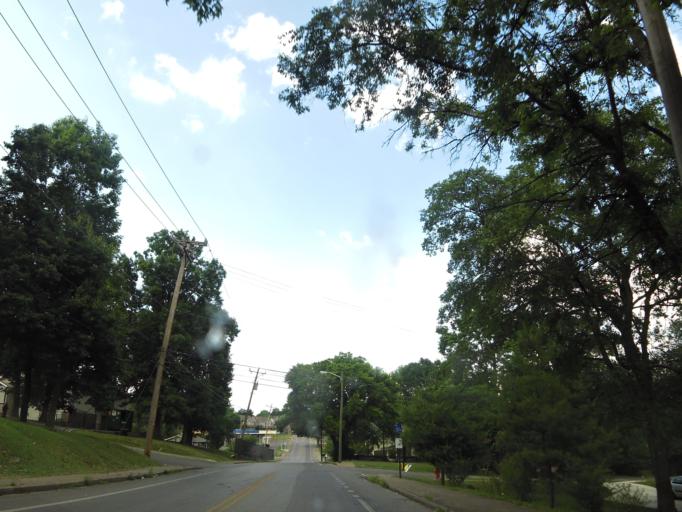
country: US
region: Tennessee
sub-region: Davidson County
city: Nashville
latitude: 36.1929
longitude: -86.7267
